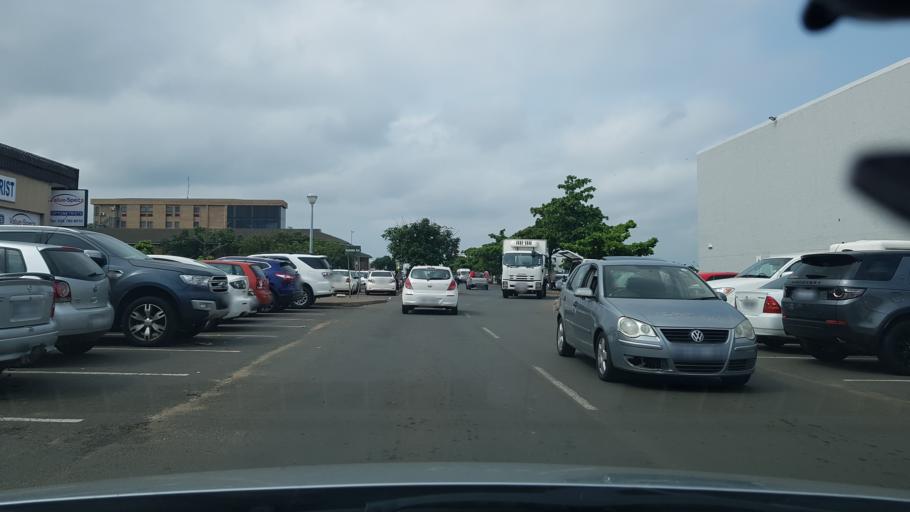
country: ZA
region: KwaZulu-Natal
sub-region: uThungulu District Municipality
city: Richards Bay
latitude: -28.7519
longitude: 32.0502
